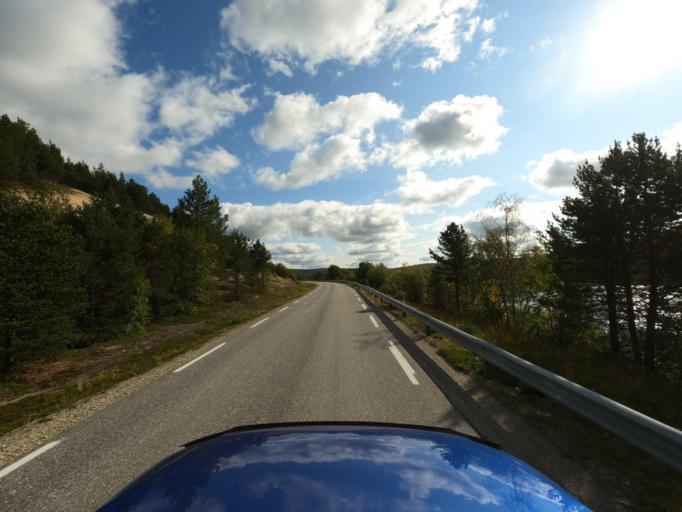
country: NO
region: Finnmark Fylke
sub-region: Karasjok
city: Karasjohka
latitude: 69.4443
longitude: 25.2141
